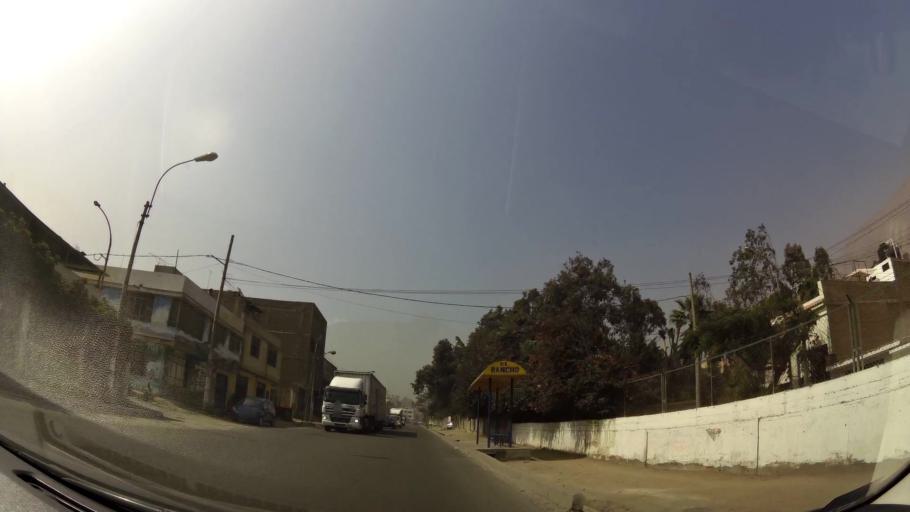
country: PE
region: Lima
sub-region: Provincia de Huarochiri
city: Ricardo Palma
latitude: -11.9217
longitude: -76.6766
